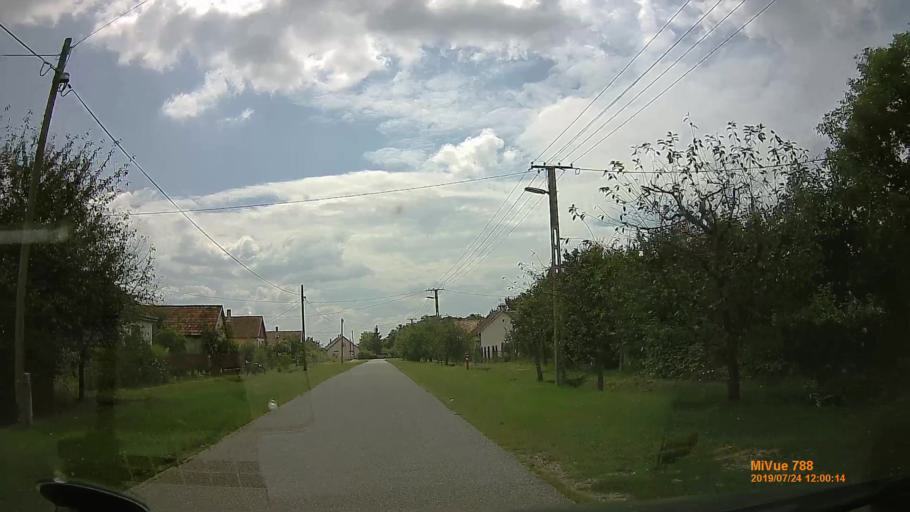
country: HU
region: Szabolcs-Szatmar-Bereg
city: Tarpa
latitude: 48.1983
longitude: 22.4517
